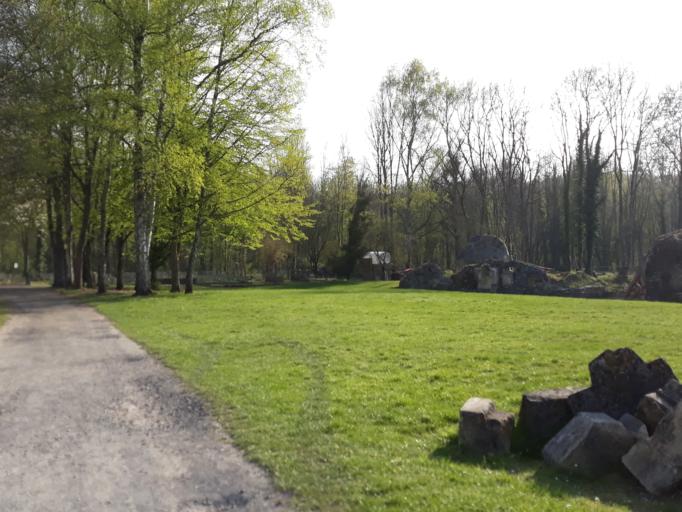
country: FR
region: Picardie
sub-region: Departement de l'Aisne
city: Bruyeres-et-Montberault
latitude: 49.4526
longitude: 3.7472
